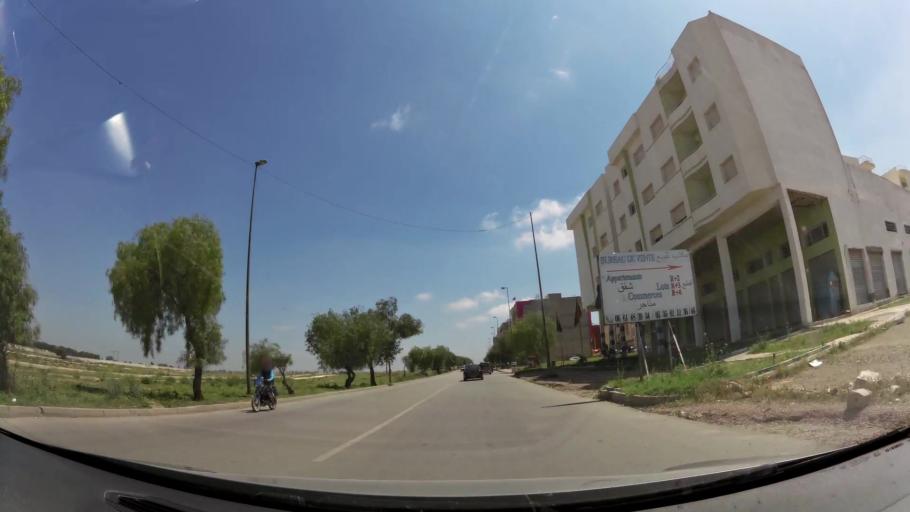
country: MA
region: Fes-Boulemane
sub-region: Fes
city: Fes
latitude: 34.0056
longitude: -5.0449
